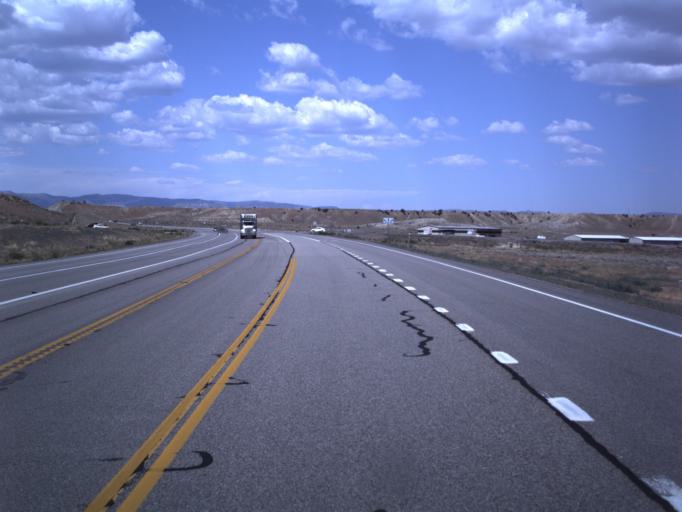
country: US
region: Utah
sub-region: Carbon County
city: Price
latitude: 39.5337
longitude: -110.8169
